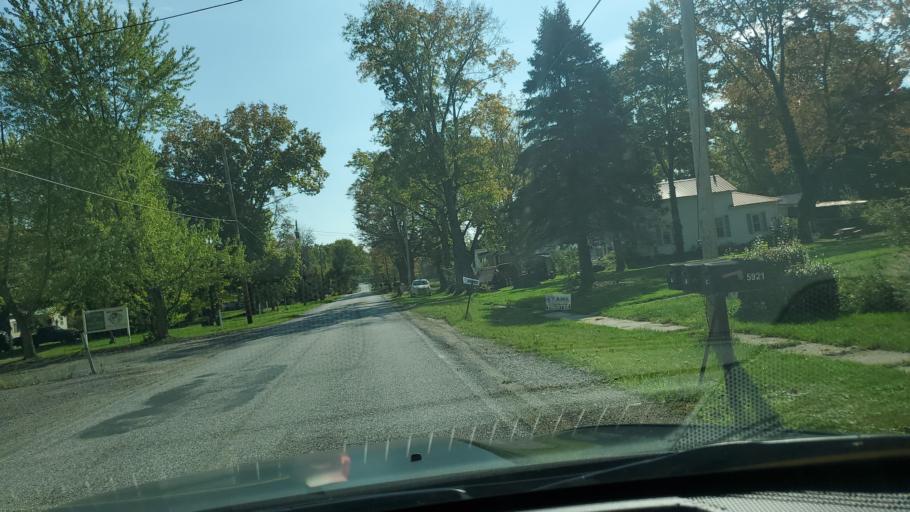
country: US
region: Ohio
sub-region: Trumbull County
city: Cortland
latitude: 41.4328
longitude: -80.6066
